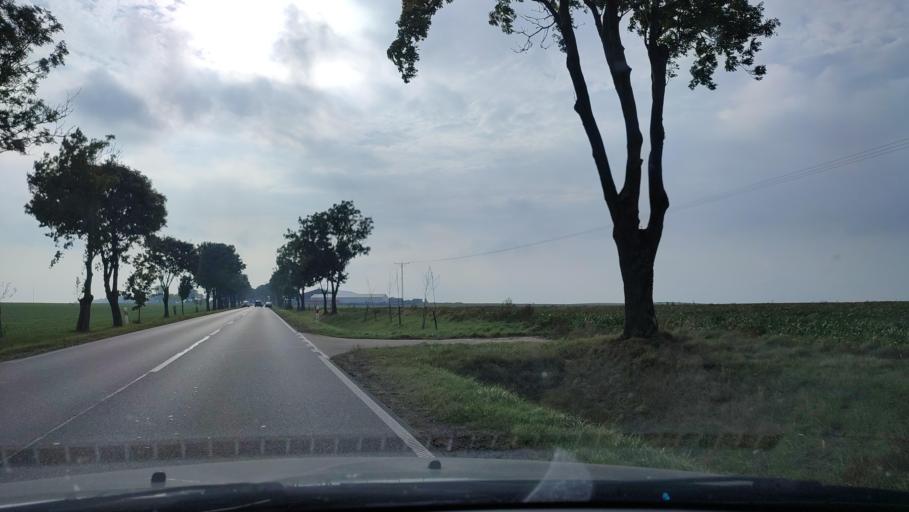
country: PL
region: Warmian-Masurian Voivodeship
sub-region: Powiat nidzicki
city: Kozlowo
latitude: 53.3311
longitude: 20.3231
